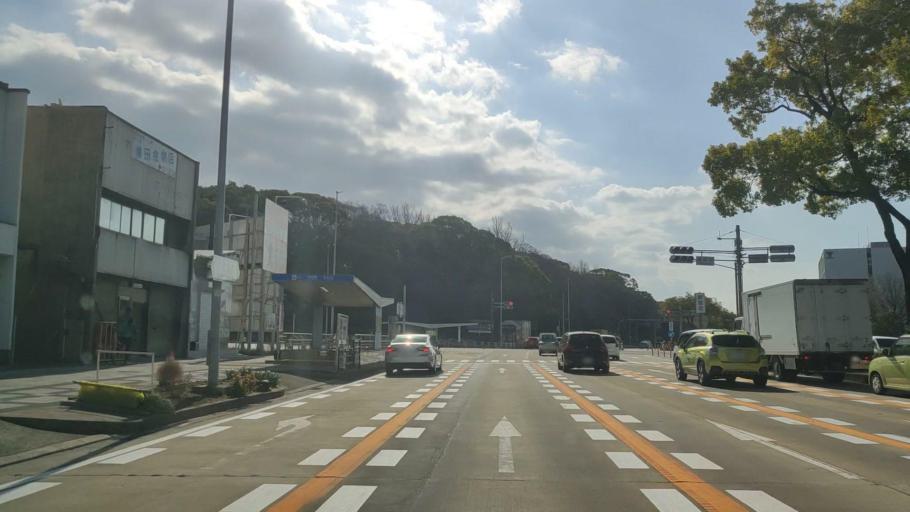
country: JP
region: Aichi
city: Nagoya-shi
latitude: 35.1286
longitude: 136.9064
